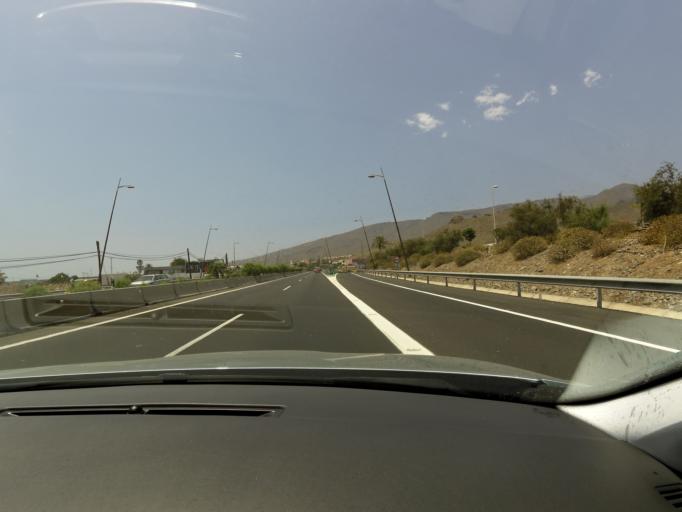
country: ES
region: Canary Islands
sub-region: Provincia de Santa Cruz de Tenerife
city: Adeje
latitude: 28.1003
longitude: -16.7308
